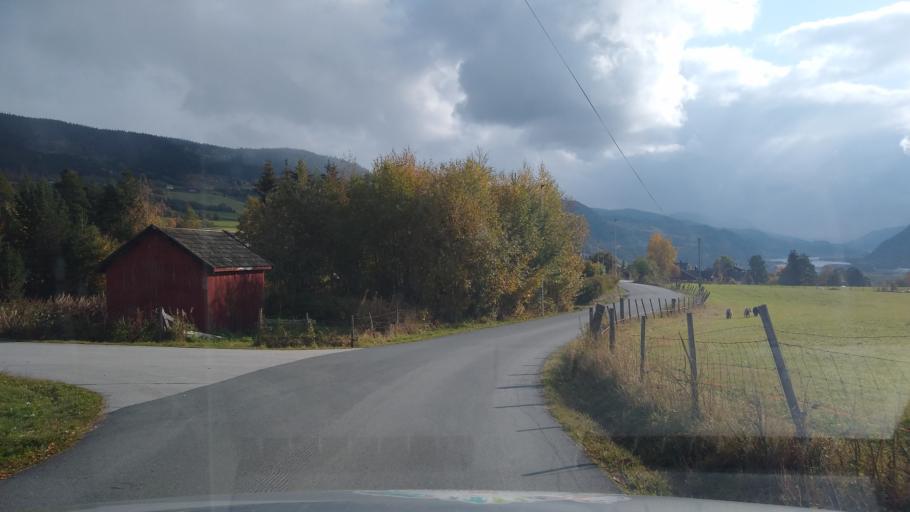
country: NO
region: Oppland
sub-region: Ringebu
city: Ringebu
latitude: 61.5385
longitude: 10.1347
